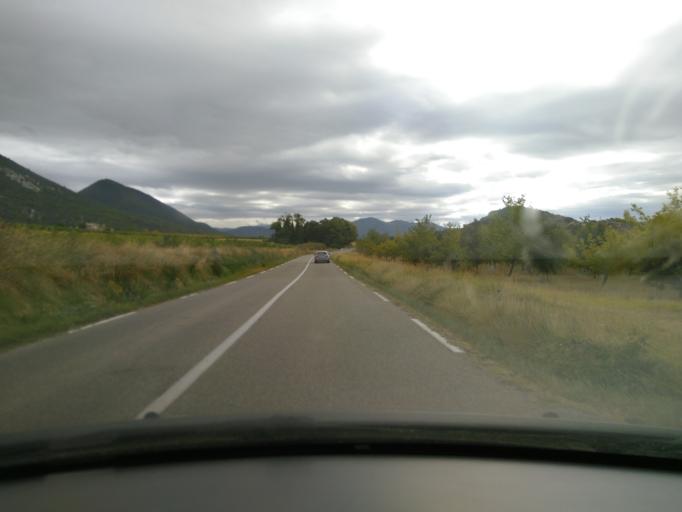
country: FR
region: Rhone-Alpes
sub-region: Departement de la Drome
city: Nyons
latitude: 44.4012
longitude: 5.0775
